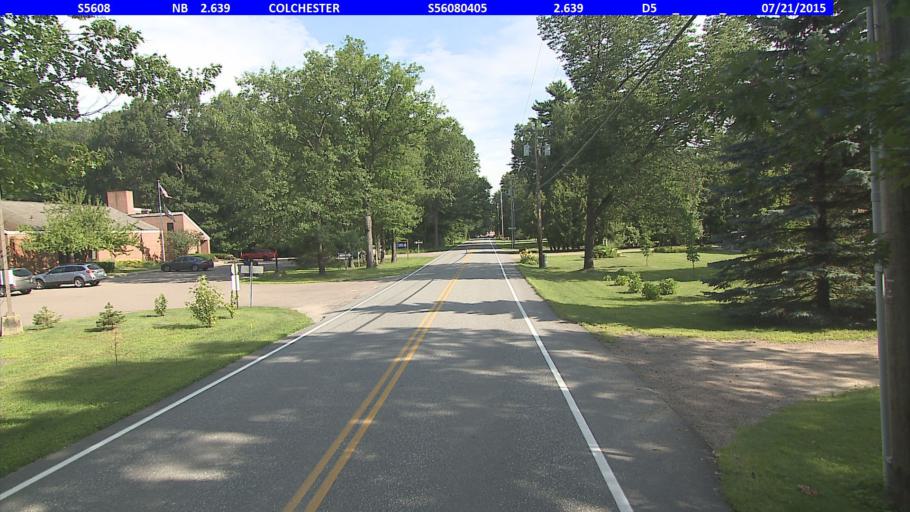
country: US
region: Vermont
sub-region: Chittenden County
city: Winooski
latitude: 44.5348
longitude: -73.2085
